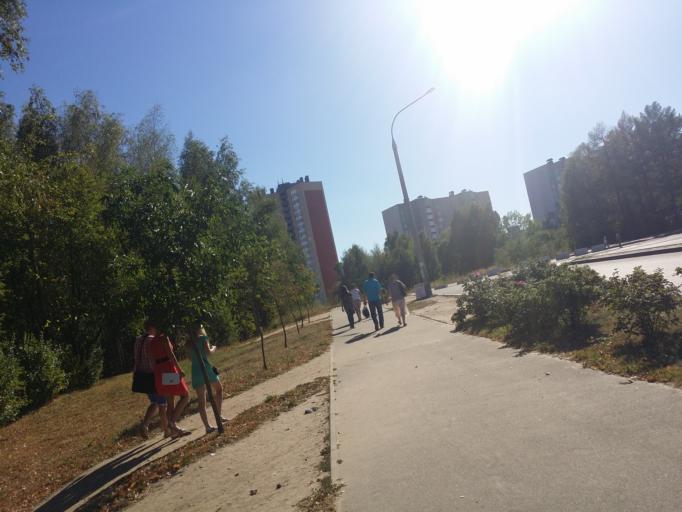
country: BY
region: Minsk
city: Vyaliki Trastsyanets
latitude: 53.8489
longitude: 27.7027
